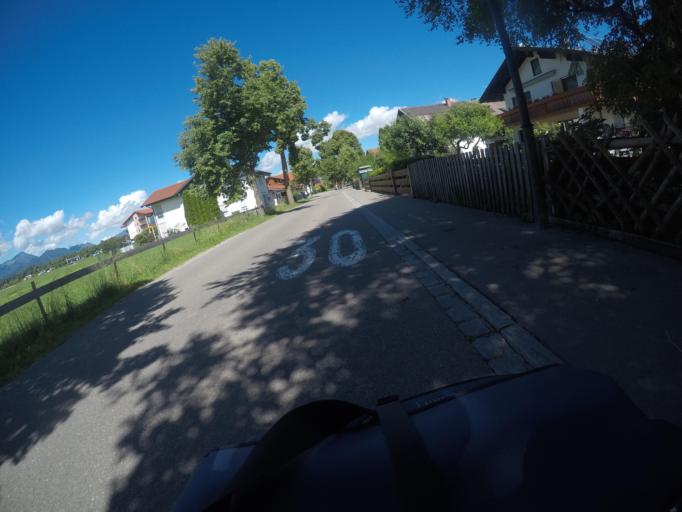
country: DE
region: Bavaria
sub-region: Swabia
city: Schwangau
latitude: 47.5808
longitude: 10.7339
